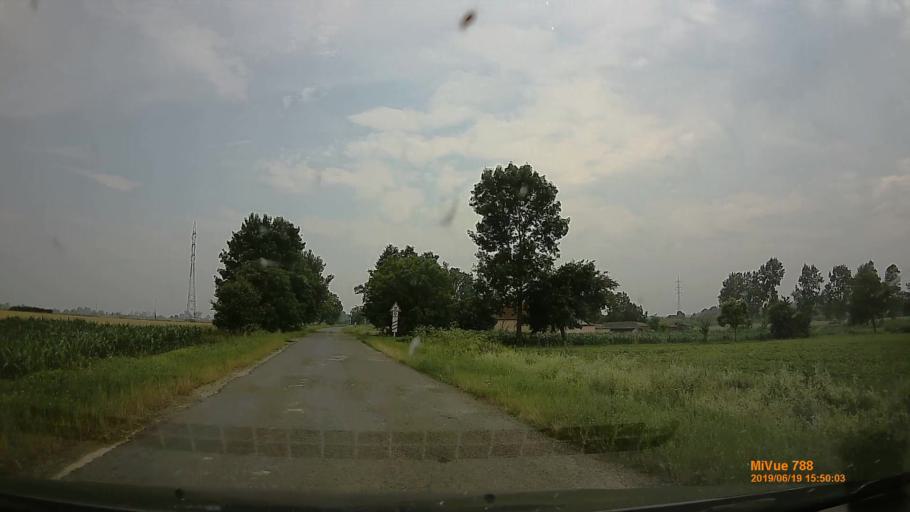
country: HU
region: Baranya
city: Szigetvar
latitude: 46.0372
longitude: 17.7482
